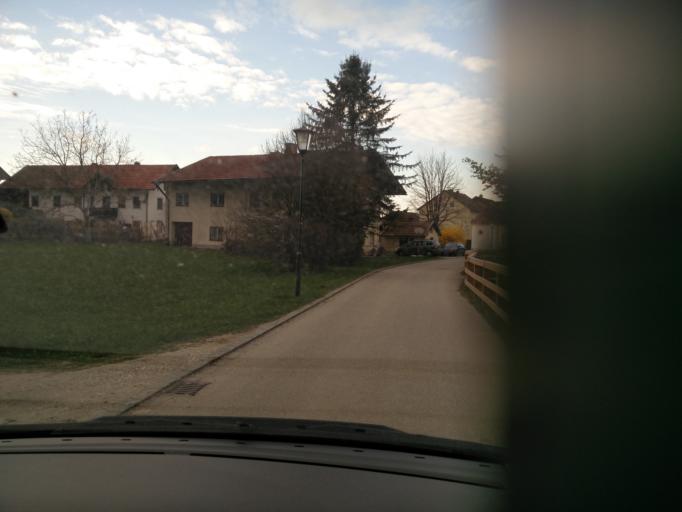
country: DE
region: Bavaria
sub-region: Upper Bavaria
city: Amerang
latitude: 47.9882
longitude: 12.3089
